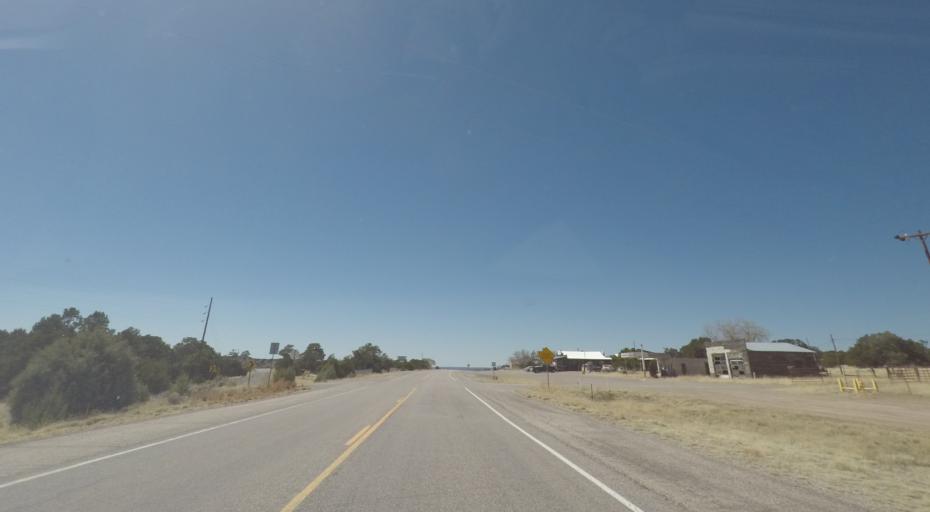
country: US
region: New Mexico
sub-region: Socorro County
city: Alamo
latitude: 34.2988
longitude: -108.1293
